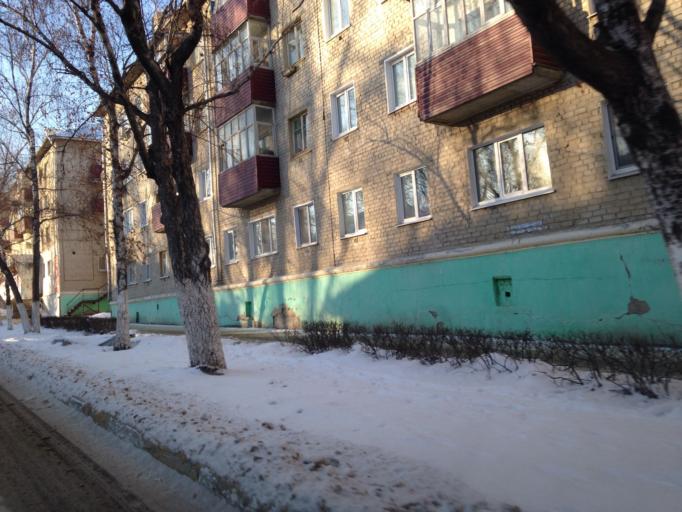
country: RU
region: Ulyanovsk
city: Novoul'yanovsk
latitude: 54.1511
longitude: 48.3824
